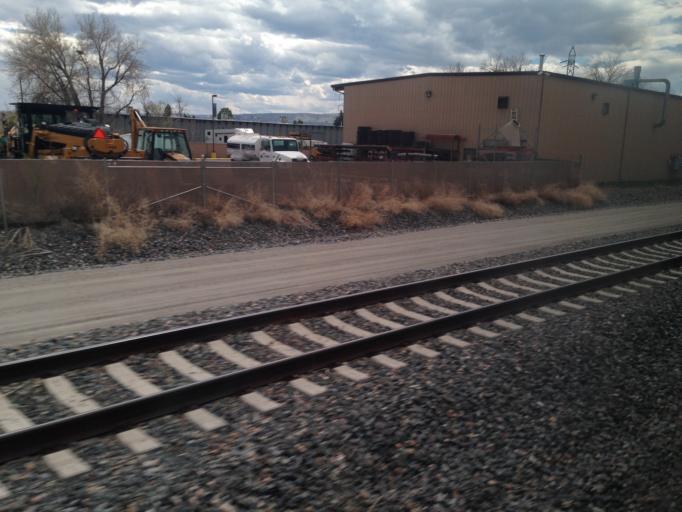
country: US
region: Colorado
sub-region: Jefferson County
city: Arvada
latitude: 39.7907
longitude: -105.1200
